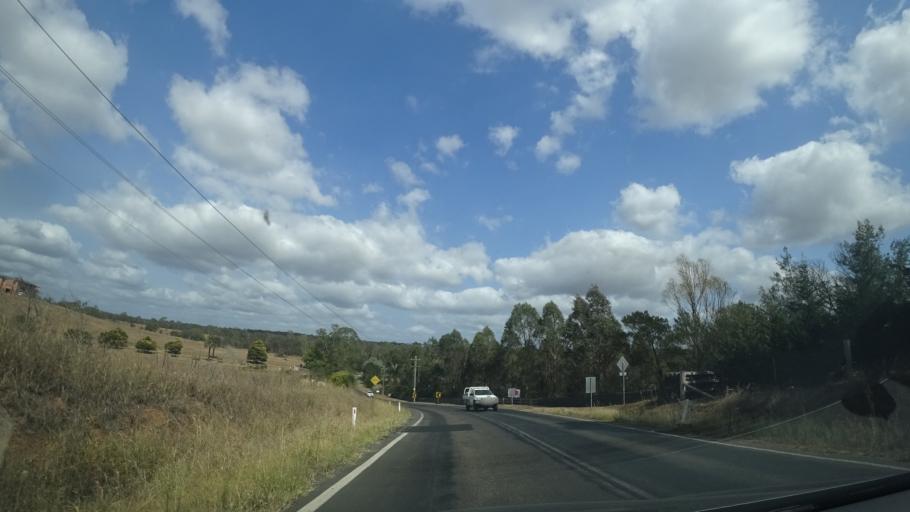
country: AU
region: New South Wales
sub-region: Wollondilly
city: Picton
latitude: -34.1858
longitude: 150.5895
